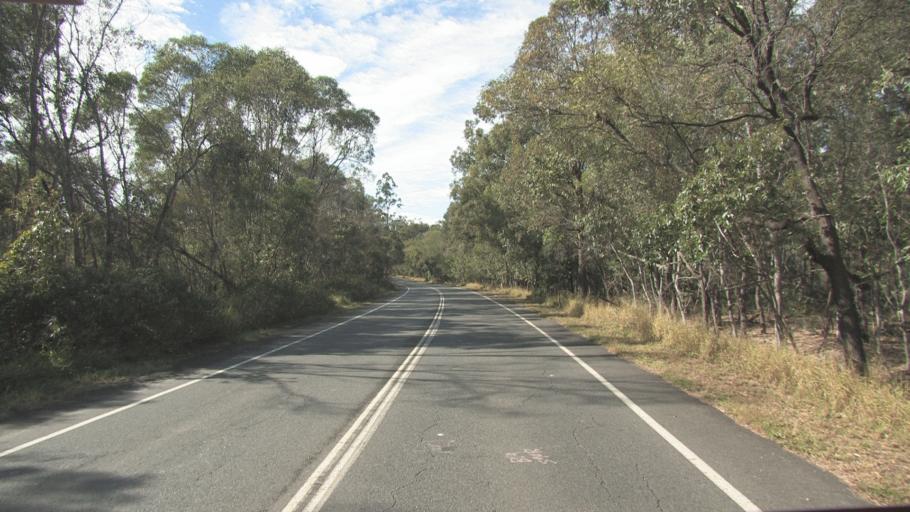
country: AU
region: Queensland
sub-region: Brisbane
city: Forest Lake
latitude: -27.6326
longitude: 152.9486
